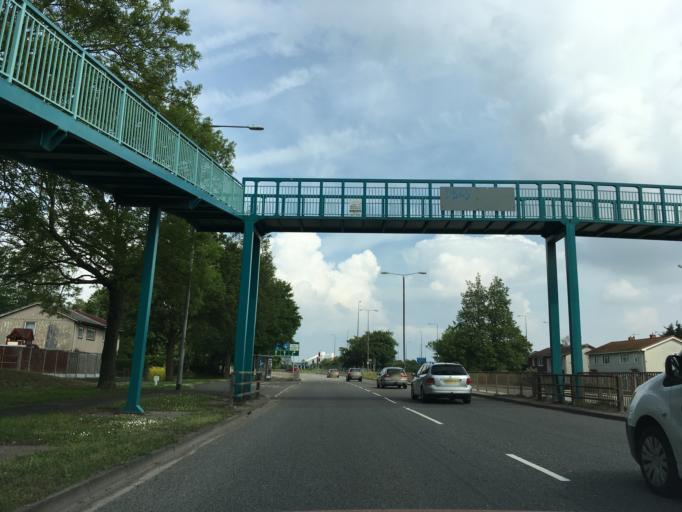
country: GB
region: England
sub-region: North Somerset
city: Easton-in-Gordano
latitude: 51.4962
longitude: -2.6898
